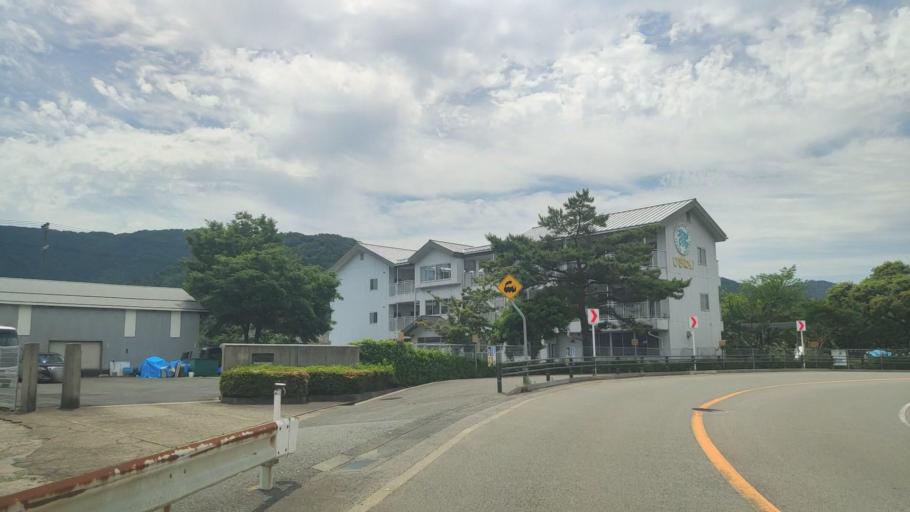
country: JP
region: Hyogo
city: Toyooka
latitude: 35.6472
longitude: 134.7586
